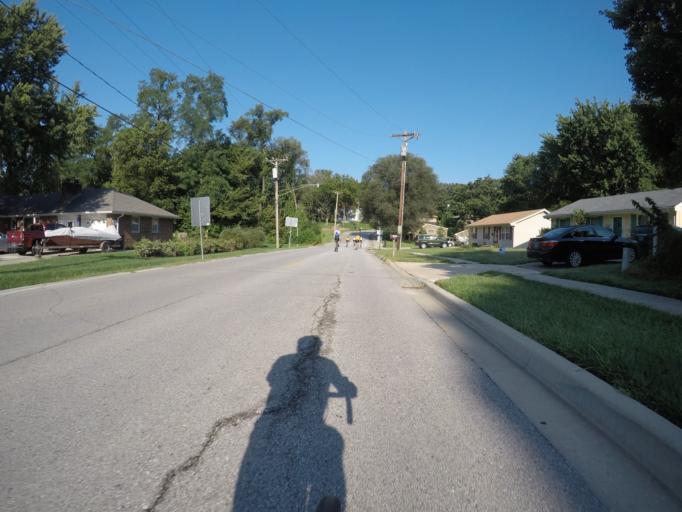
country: US
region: Missouri
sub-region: Platte County
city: Weston
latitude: 39.4117
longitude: -94.8955
